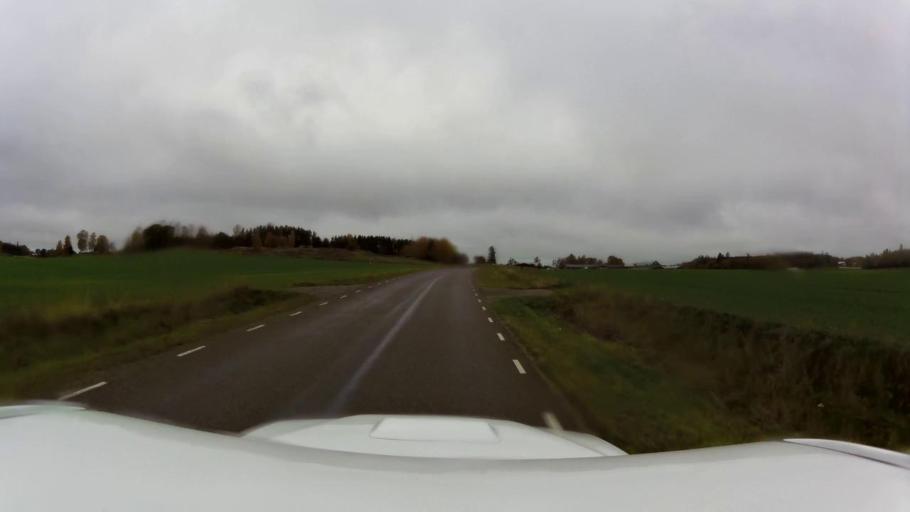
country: SE
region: OEstergoetland
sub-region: Linkopings Kommun
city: Linghem
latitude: 58.4733
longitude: 15.8195
